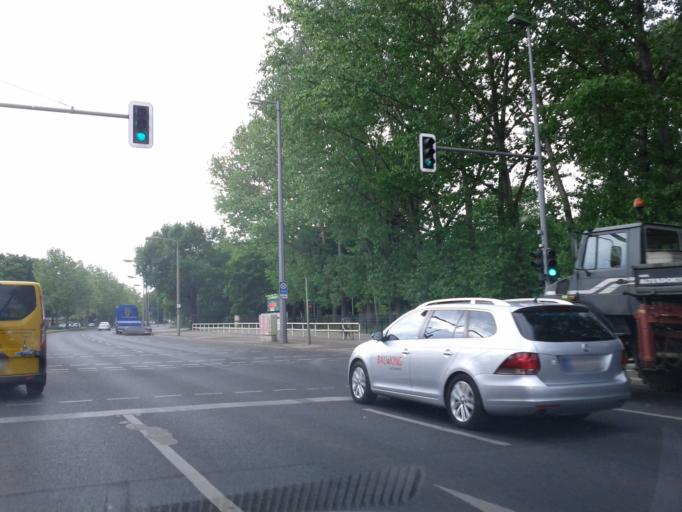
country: DE
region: Berlin
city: Adlershof
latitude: 52.4577
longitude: 13.5437
